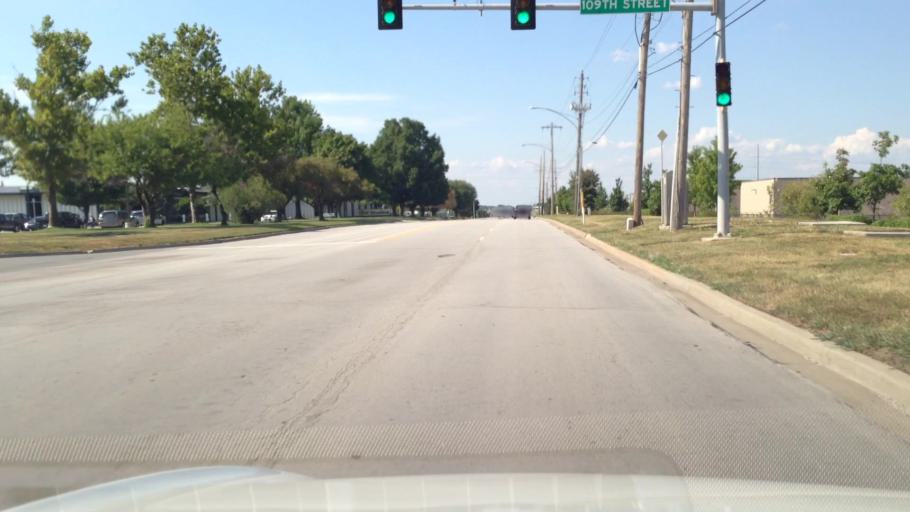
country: US
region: Kansas
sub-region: Johnson County
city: Lenexa
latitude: 38.9309
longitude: -94.7608
